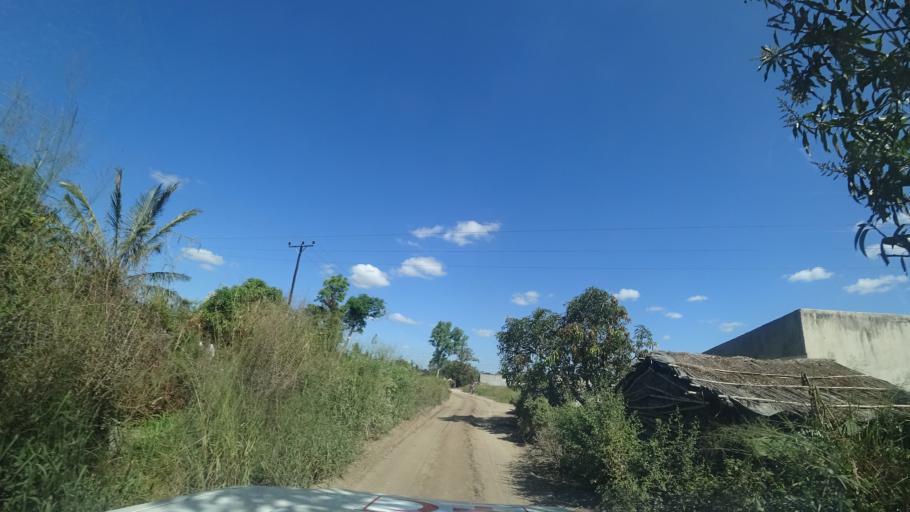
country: MZ
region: Sofala
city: Dondo
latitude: -19.4933
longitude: 34.5989
